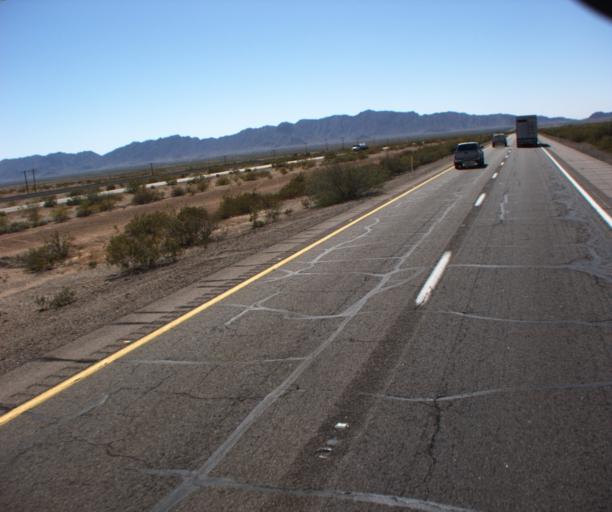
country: US
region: Arizona
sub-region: Yuma County
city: Wellton
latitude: 32.7602
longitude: -113.6376
